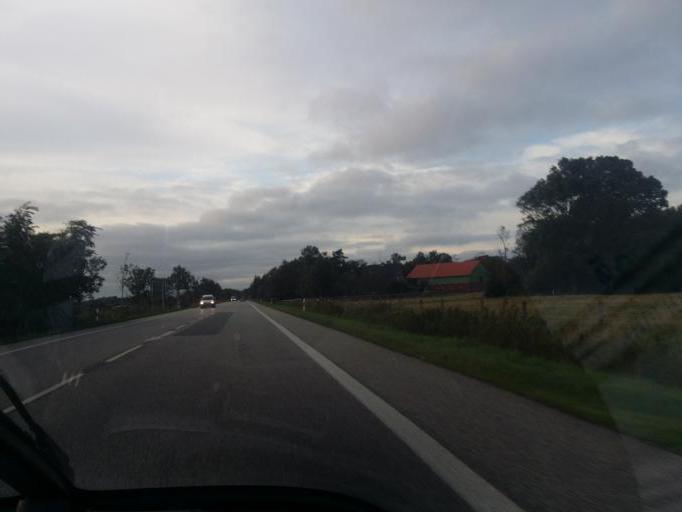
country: DE
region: Schleswig-Holstein
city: Bargum
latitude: 54.7292
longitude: 8.9541
